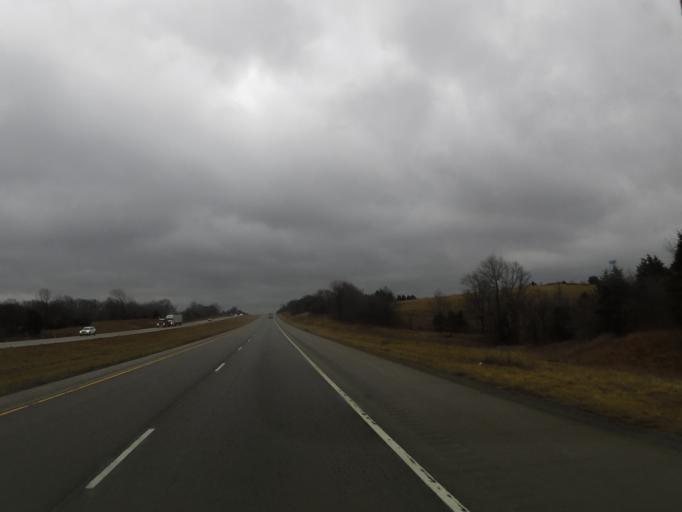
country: US
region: Illinois
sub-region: Johnson County
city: Goreville
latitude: 37.5758
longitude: -88.9608
